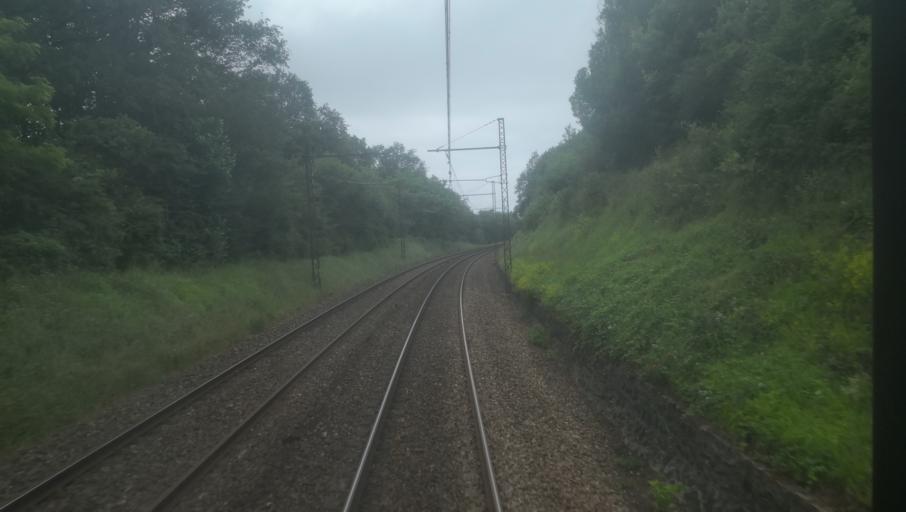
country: FR
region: Centre
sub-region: Departement de l'Indre
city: Le Pechereau
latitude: 46.4954
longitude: 1.5263
